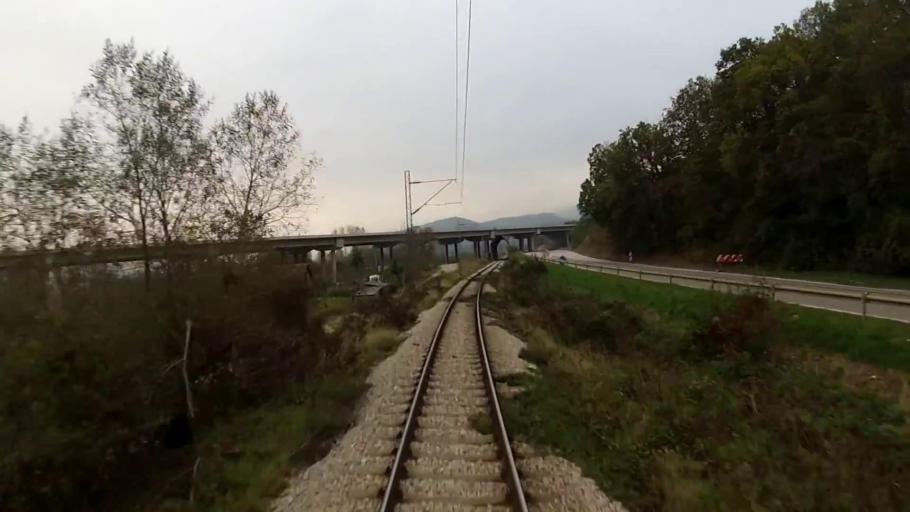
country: RS
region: Central Serbia
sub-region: Pirotski Okrug
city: Dimitrovgrad
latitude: 43.0079
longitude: 22.8043
